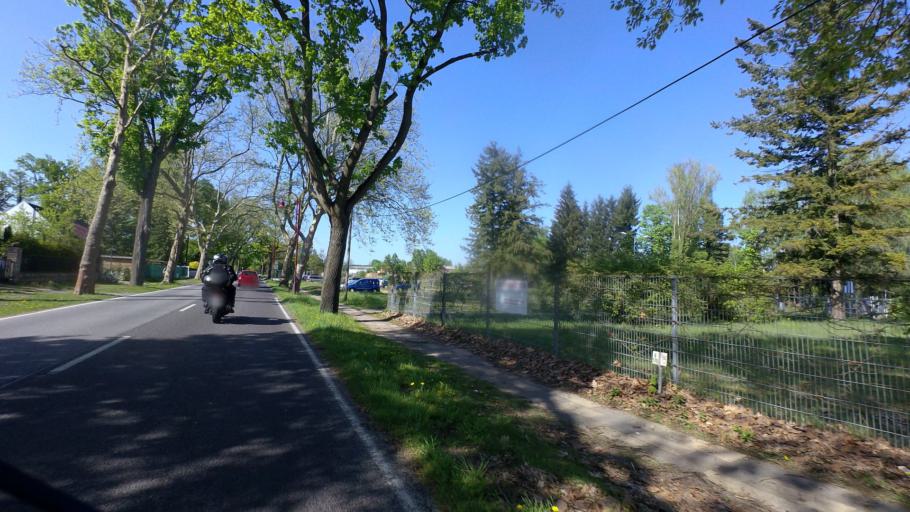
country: DE
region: Brandenburg
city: Bestensee
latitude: 52.2346
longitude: 13.6675
